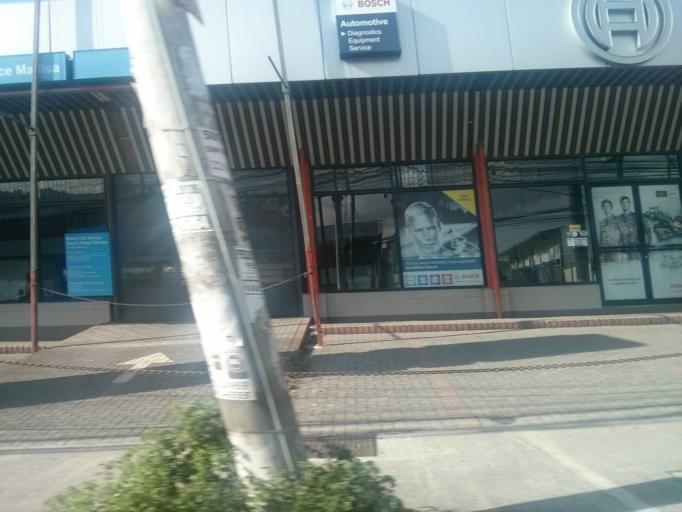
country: CR
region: San Jose
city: Colima
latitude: 9.9484
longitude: -84.0943
